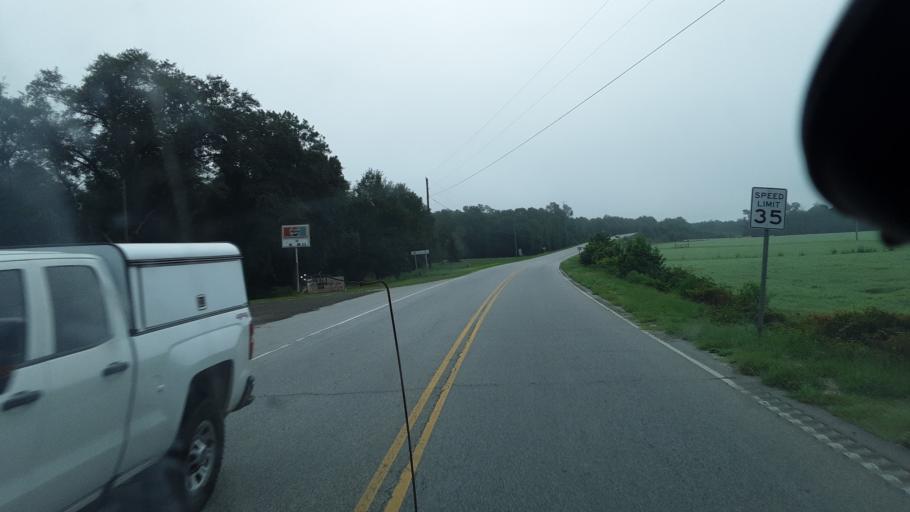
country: US
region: South Carolina
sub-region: Florence County
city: Johnsonville
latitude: 33.9140
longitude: -79.4192
